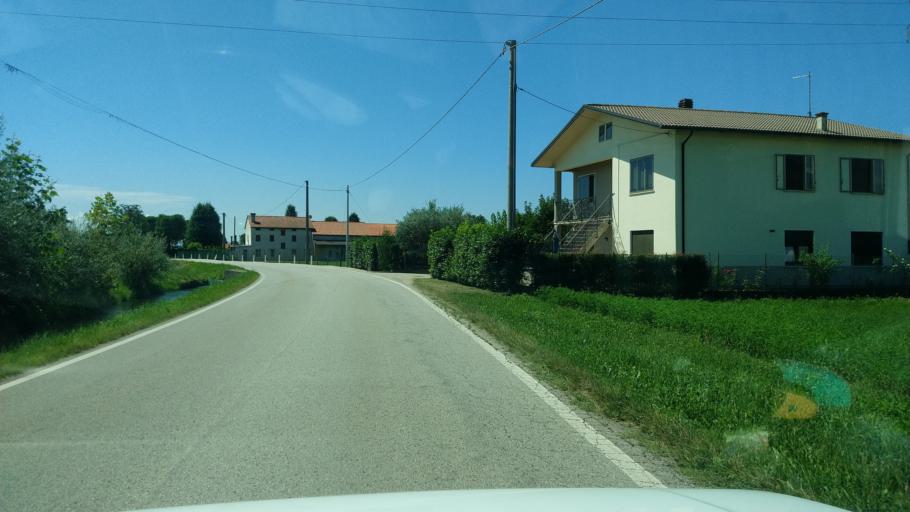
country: IT
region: Veneto
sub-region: Provincia di Vicenza
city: Preara-Moraro-Leva Nord
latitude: 45.6916
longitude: 11.5391
